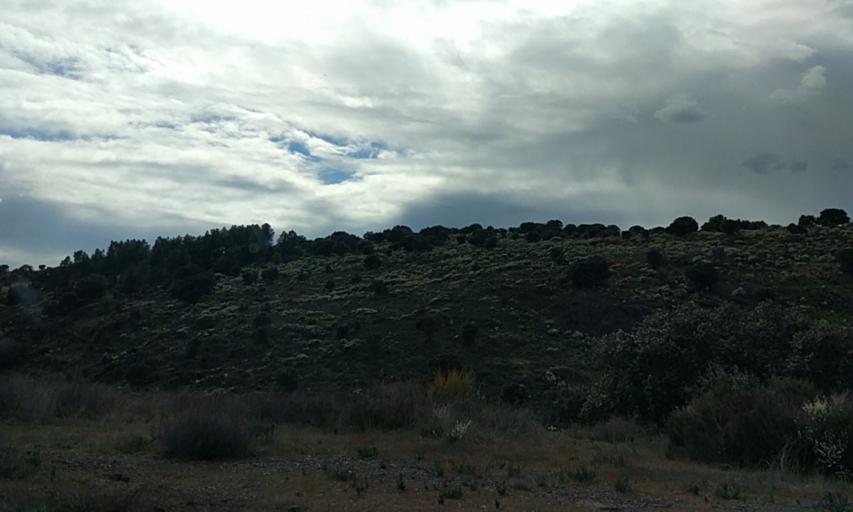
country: ES
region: Castille and Leon
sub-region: Provincia de Salamanca
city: Herguijuela de Ciudad Rodrigo
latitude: 40.4965
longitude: -6.5792
